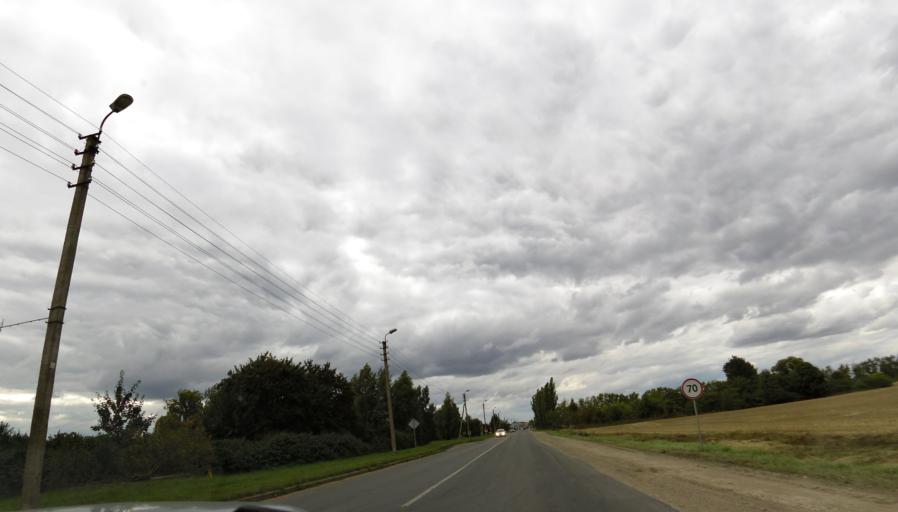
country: LT
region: Panevezys
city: Pasvalys
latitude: 56.0699
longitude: 24.3999
